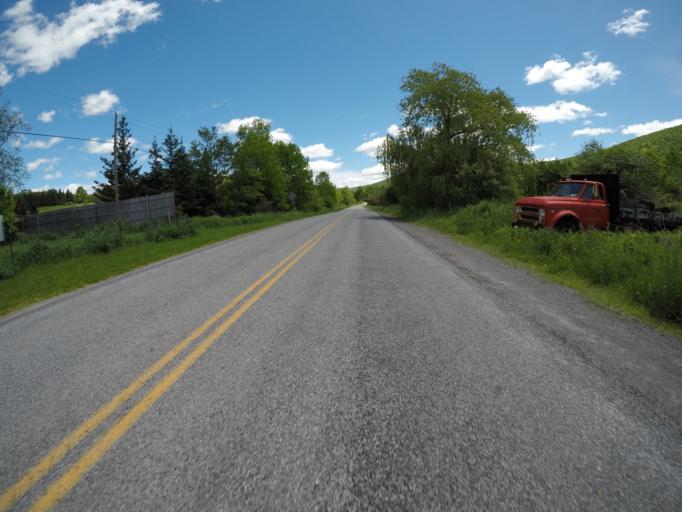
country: US
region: New York
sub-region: Delaware County
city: Stamford
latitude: 42.2424
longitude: -74.5503
